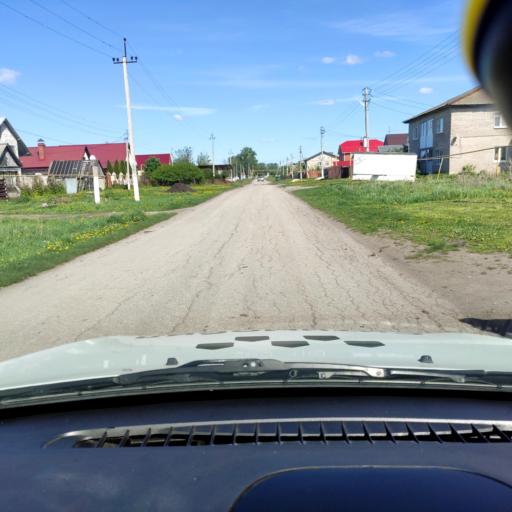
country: RU
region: Samara
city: Tol'yatti
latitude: 53.6770
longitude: 49.4201
